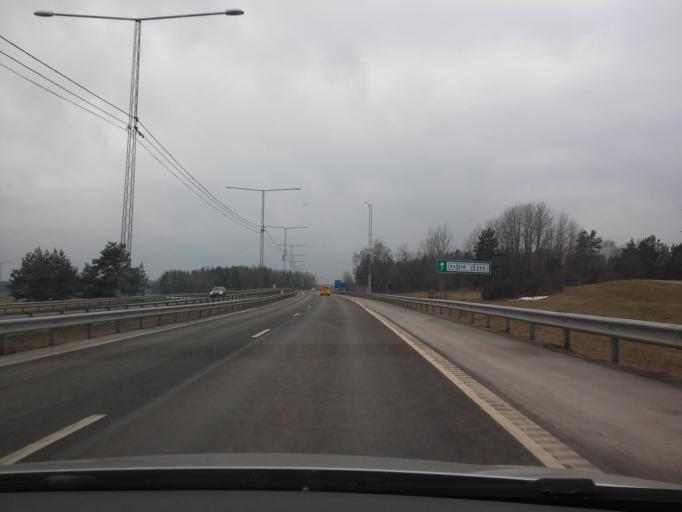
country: SE
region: Stockholm
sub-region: Taby Kommun
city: Taby
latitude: 59.4664
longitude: 18.1505
